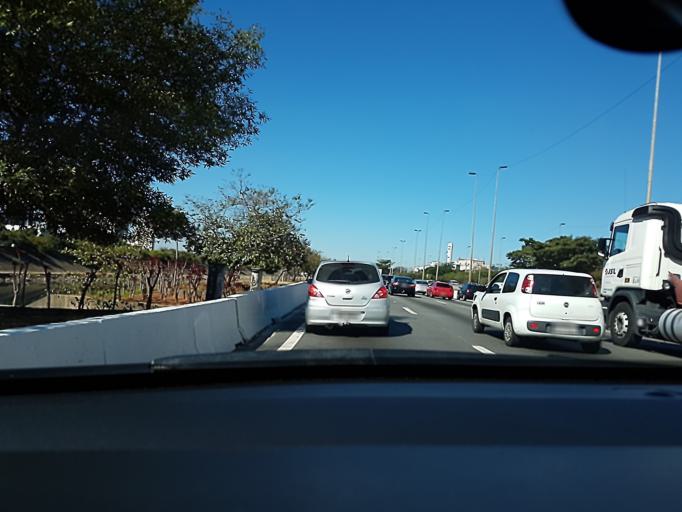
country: BR
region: Sao Paulo
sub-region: Sao Paulo
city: Sao Paulo
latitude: -23.5161
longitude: -46.6637
